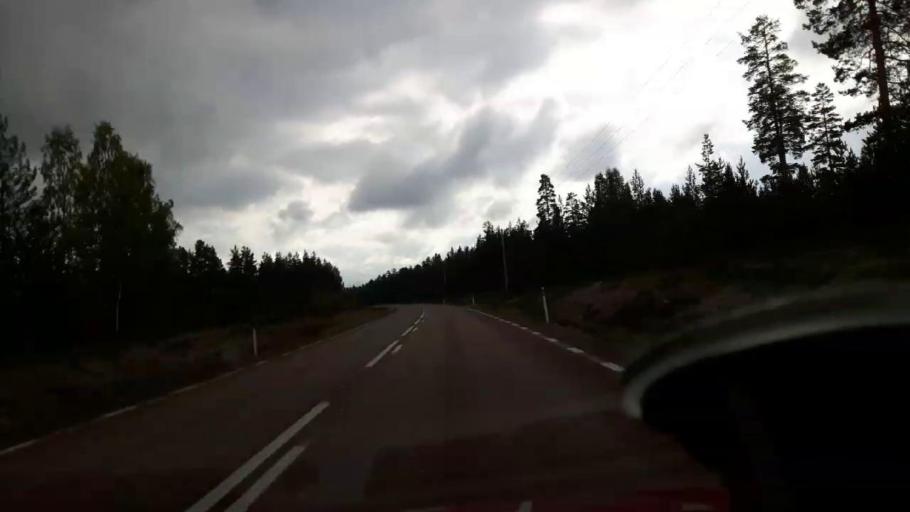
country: SE
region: Gaevleborg
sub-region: Soderhamns Kommun
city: Ljusne
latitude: 61.1118
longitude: 16.9355
